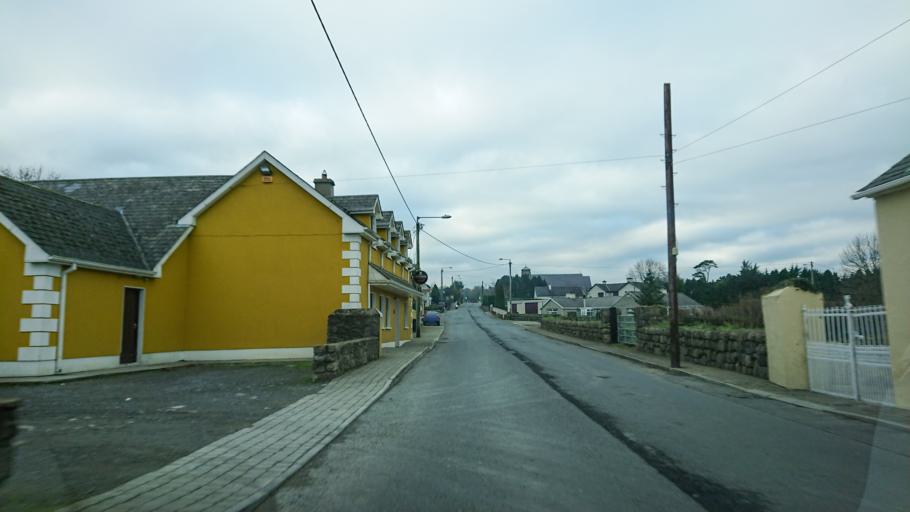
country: IE
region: Munster
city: Carrick-on-Suir
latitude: 52.3051
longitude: -7.4952
